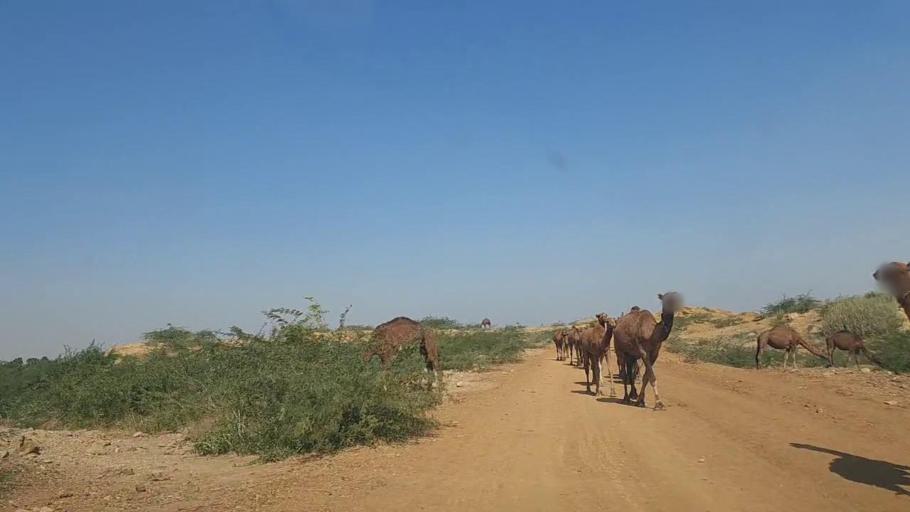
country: PK
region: Sindh
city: Thatta
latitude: 24.8331
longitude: 68.0194
